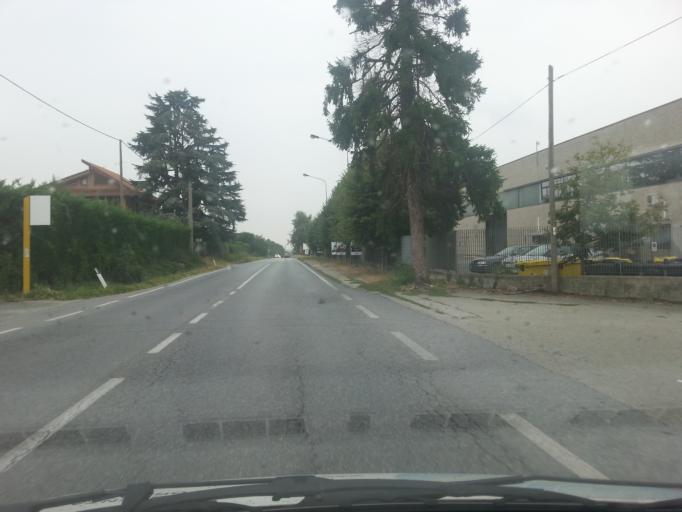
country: IT
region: Piedmont
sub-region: Provincia di Torino
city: Rivalta di Torino
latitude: 45.0435
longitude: 7.5222
